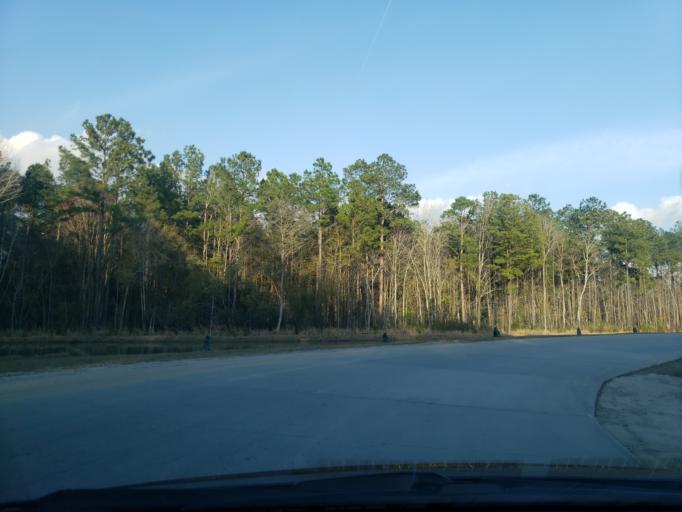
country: US
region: Georgia
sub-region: Chatham County
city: Bloomingdale
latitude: 32.1515
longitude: -81.2874
